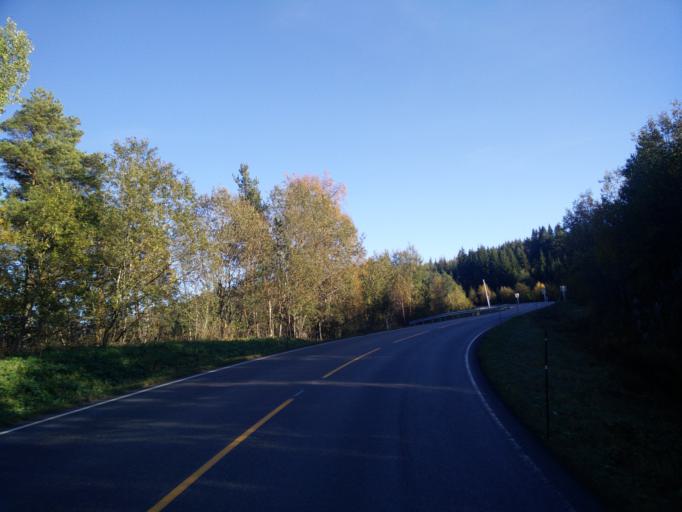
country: NO
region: More og Romsdal
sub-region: Halsa
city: Liaboen
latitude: 63.0739
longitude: 8.3016
